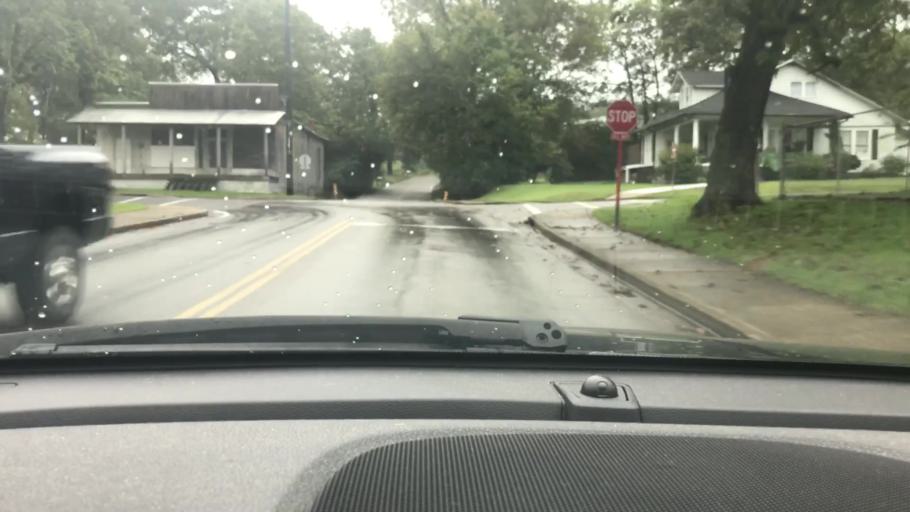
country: US
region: Tennessee
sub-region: Cheatham County
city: Kingston Springs
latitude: 36.0996
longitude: -87.1151
